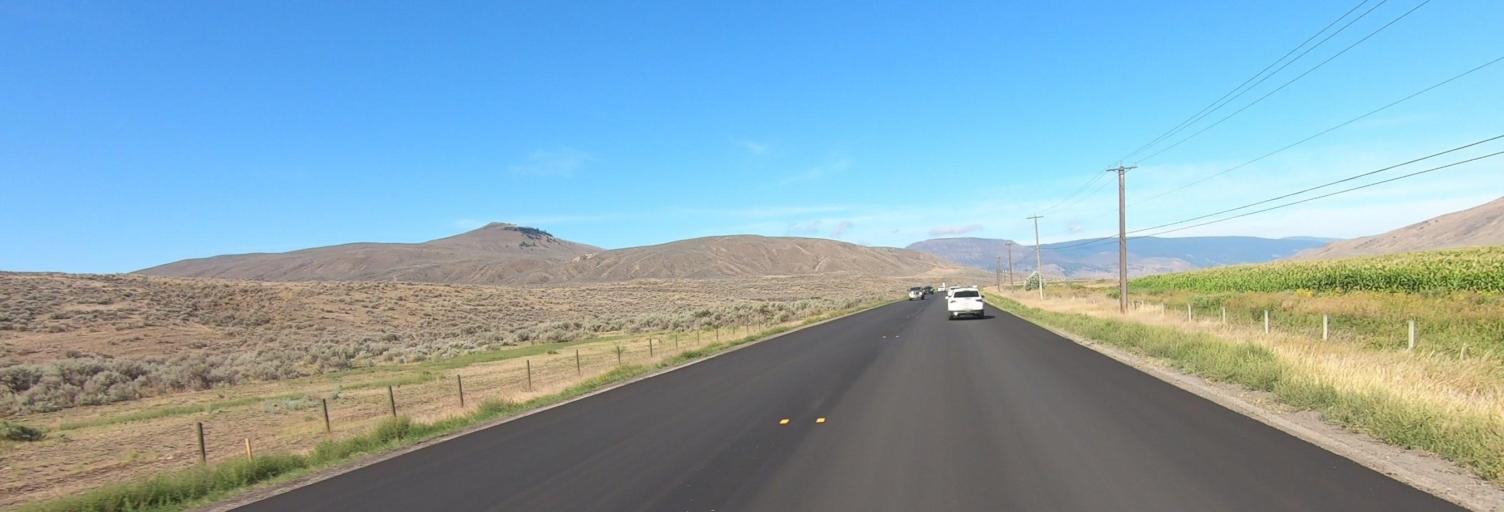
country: CA
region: British Columbia
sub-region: Thompson-Nicola Regional District
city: Ashcroft
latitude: 50.7858
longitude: -121.2120
